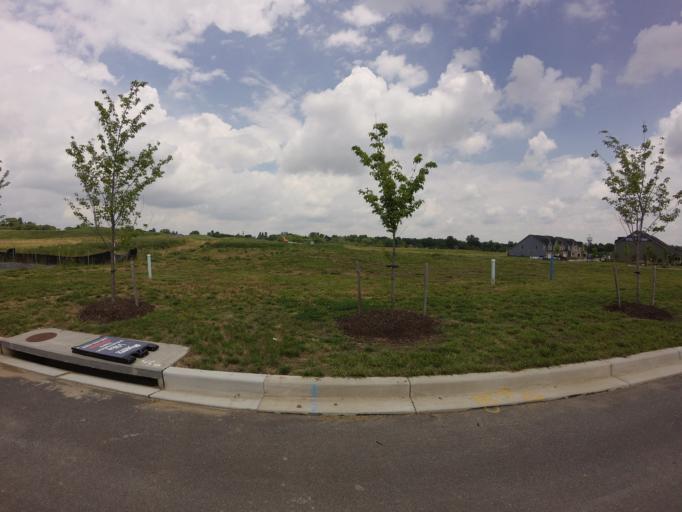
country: US
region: Maryland
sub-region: Frederick County
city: Brunswick
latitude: 39.3262
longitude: -77.6306
